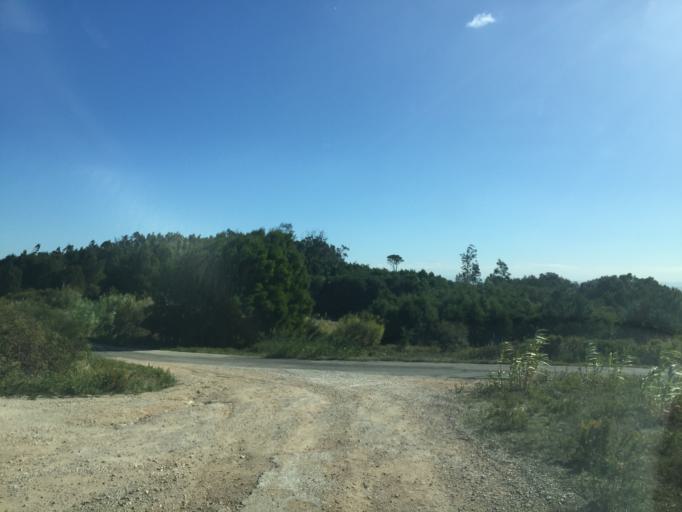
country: PT
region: Coimbra
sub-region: Figueira da Foz
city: Tavarede
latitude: 40.1956
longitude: -8.8538
